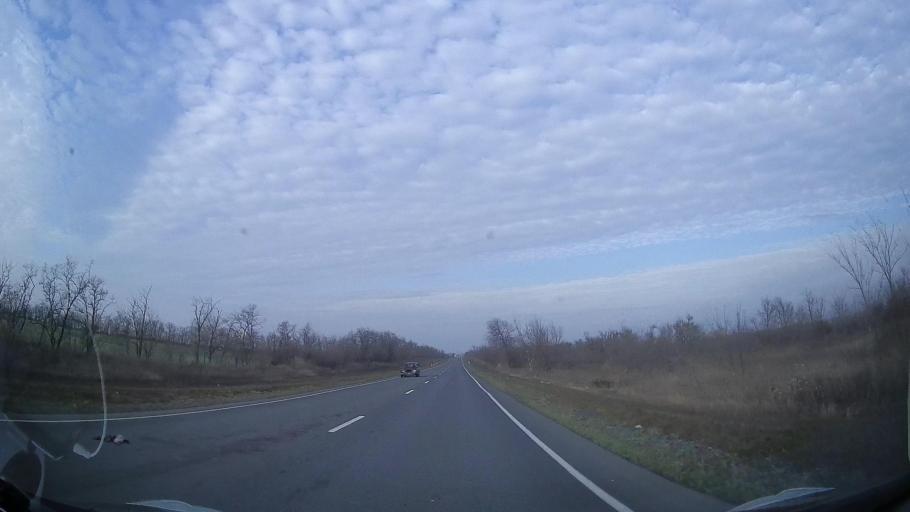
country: RU
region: Rostov
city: Bagayevskaya
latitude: 47.1511
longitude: 40.2765
